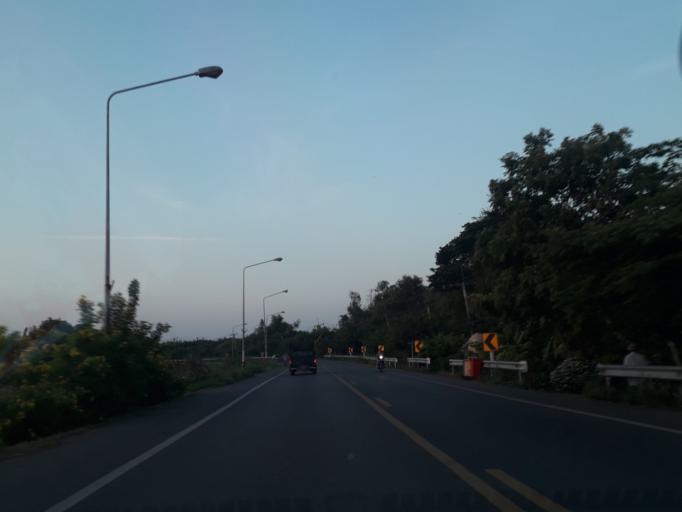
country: TH
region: Phra Nakhon Si Ayutthaya
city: Maha Rat
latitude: 14.5585
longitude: 100.5398
